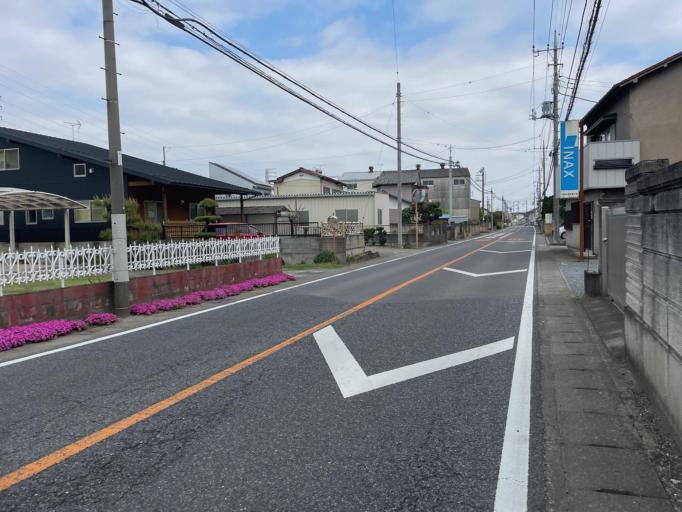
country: JP
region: Gunma
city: Isesaki
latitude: 36.2883
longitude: 139.1781
